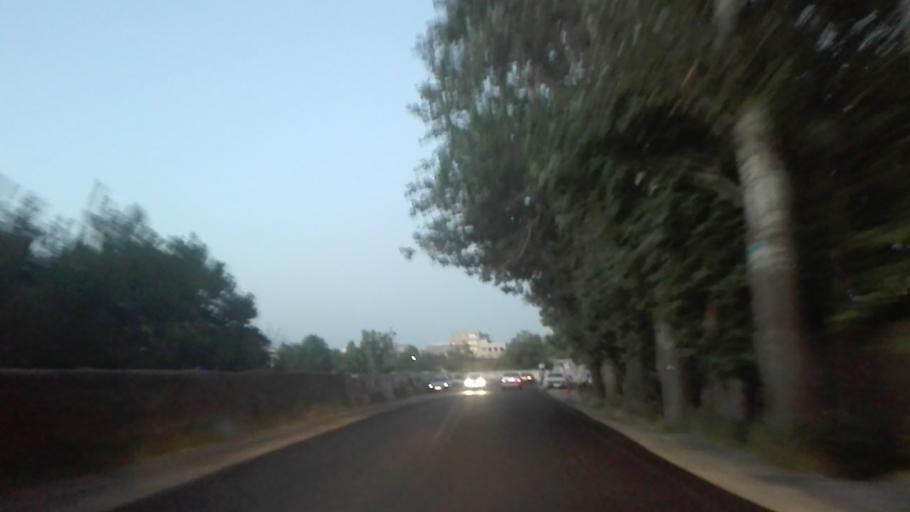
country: IR
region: Tehran
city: Shahriar
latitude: 35.6414
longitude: 51.0590
